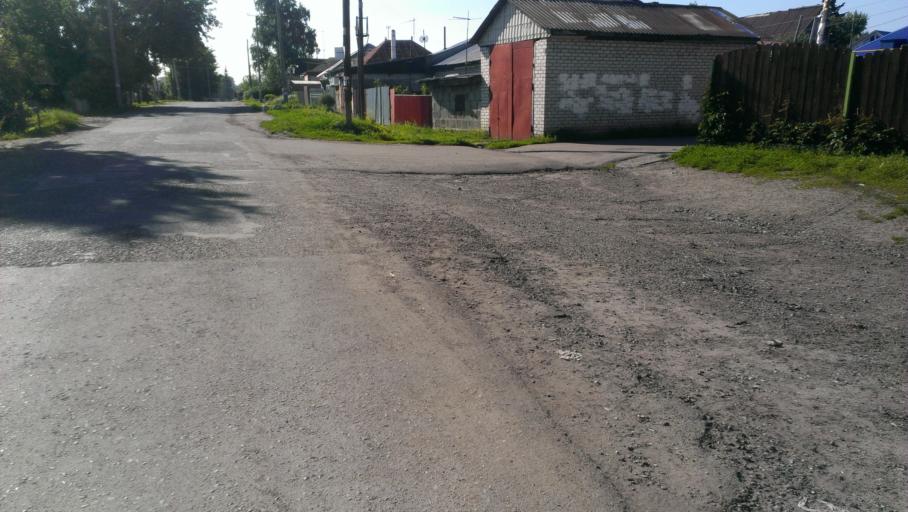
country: RU
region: Altai Krai
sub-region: Gorod Barnaulskiy
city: Barnaul
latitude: 53.3546
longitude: 83.7530
